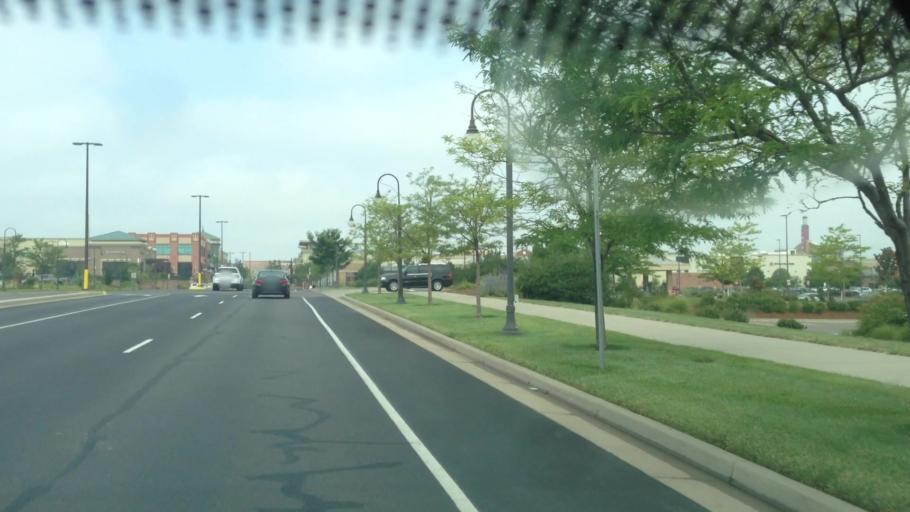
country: US
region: Colorado
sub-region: Douglas County
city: Parker
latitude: 39.6046
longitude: -104.7048
